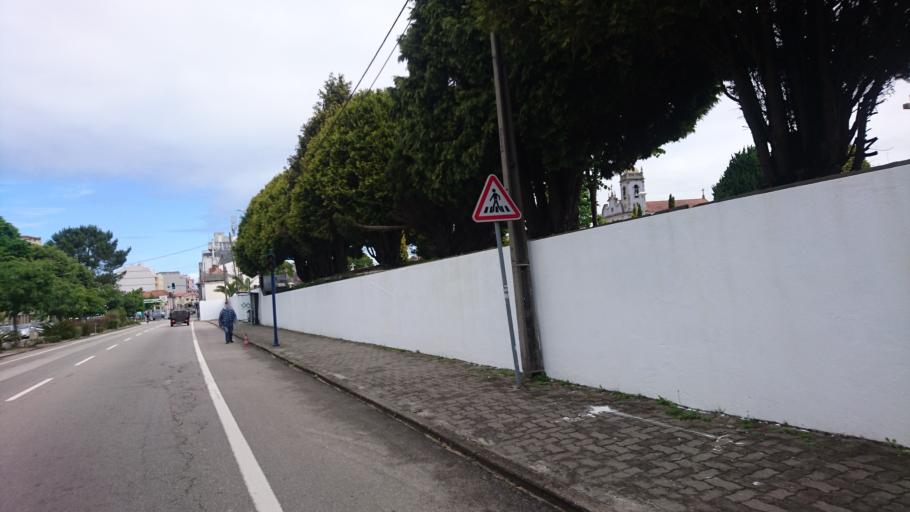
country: PT
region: Aveiro
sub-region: Ovar
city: Esmoriz
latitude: 40.9545
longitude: -8.6256
